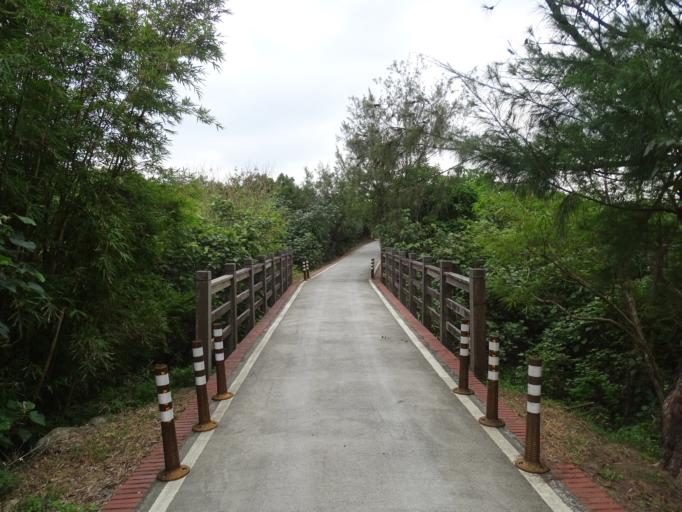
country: TW
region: Taiwan
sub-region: Keelung
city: Keelung
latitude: 25.0343
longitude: 121.9306
